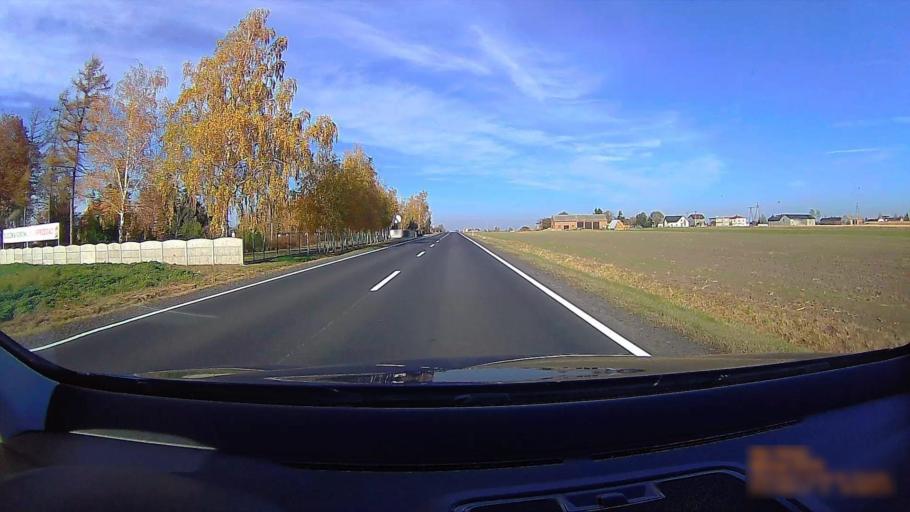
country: PL
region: Greater Poland Voivodeship
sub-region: Kalisz
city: Kalisz
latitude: 51.8301
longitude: 18.0949
